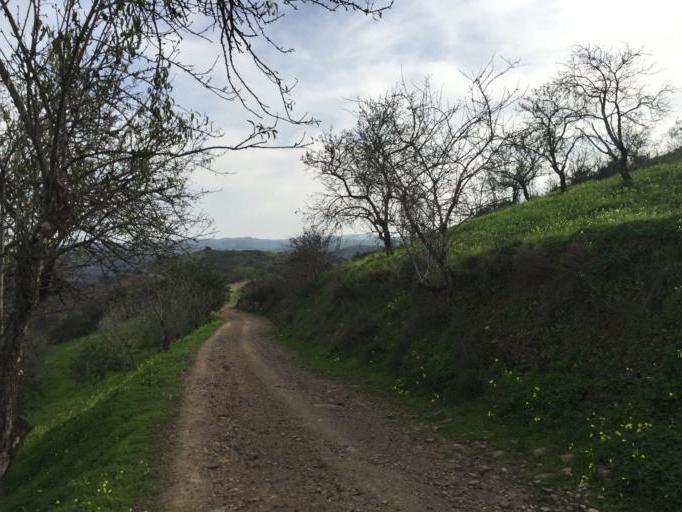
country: PT
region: Faro
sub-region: Tavira
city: Tavira
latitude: 37.2992
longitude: -7.6161
